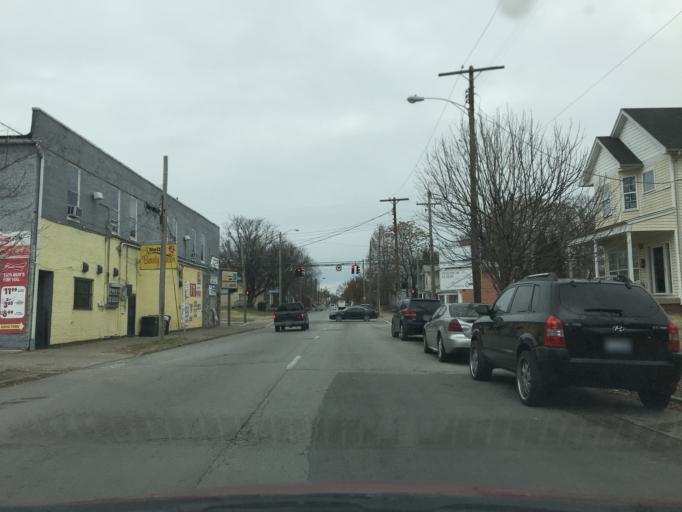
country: US
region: Kentucky
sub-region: Jefferson County
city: Louisville
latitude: 38.2538
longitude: -85.7857
